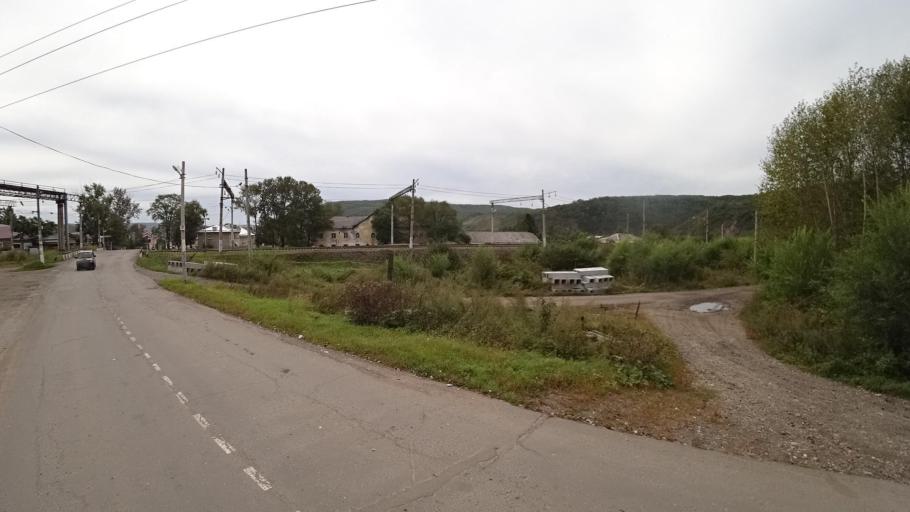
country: RU
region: Jewish Autonomous Oblast
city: Khingansk
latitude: 49.0176
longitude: 131.0547
